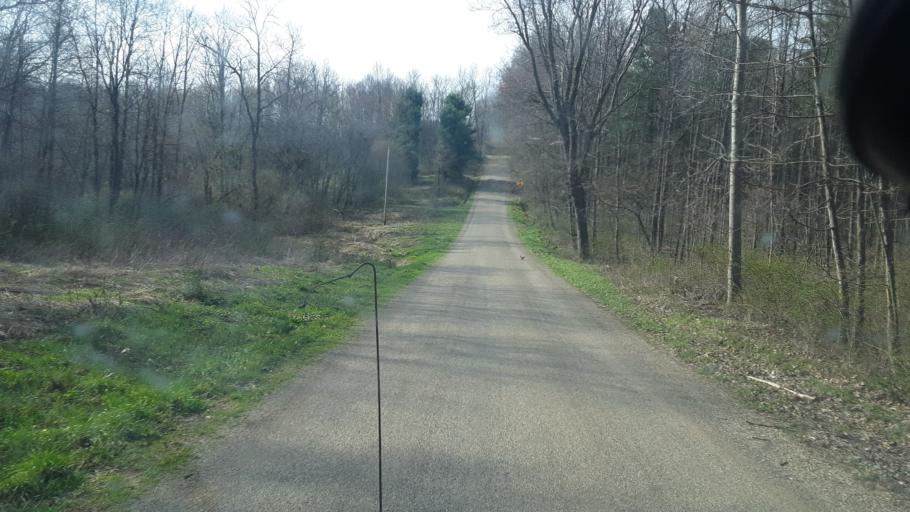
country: US
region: Ohio
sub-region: Ashland County
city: Loudonville
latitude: 40.5752
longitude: -82.3422
